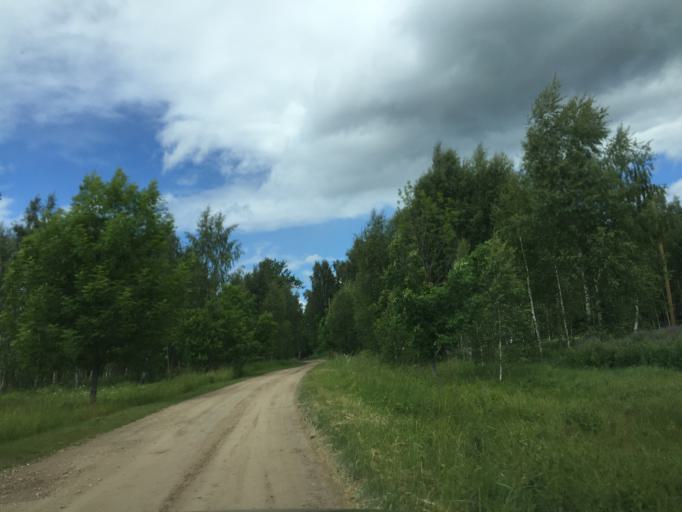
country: LV
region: Lecava
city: Iecava
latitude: 56.5741
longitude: 24.1131
